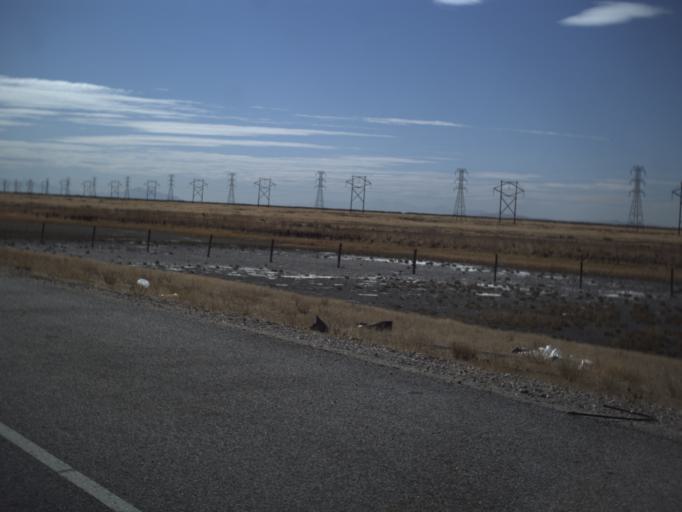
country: US
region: Utah
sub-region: Box Elder County
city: Brigham City
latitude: 41.5093
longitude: -112.0631
